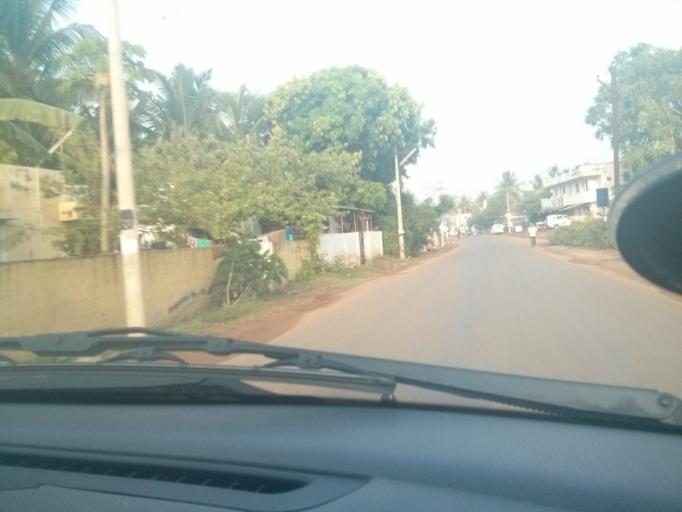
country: IN
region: Tamil Nadu
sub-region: Coimbatore
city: Coimbatore
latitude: 11.0357
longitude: 76.9171
